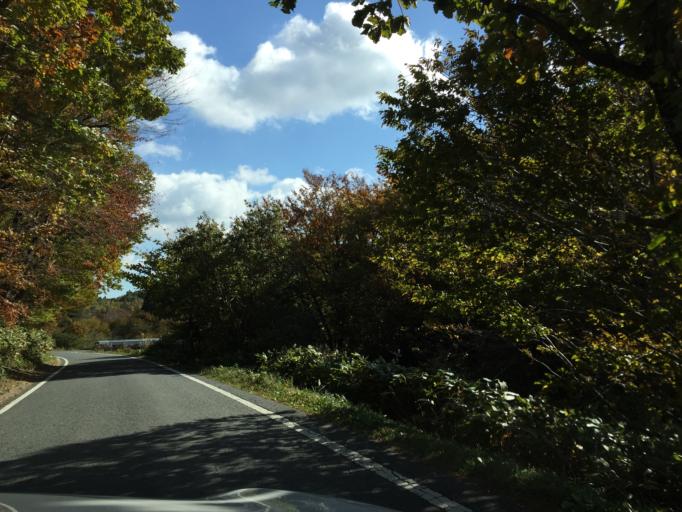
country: JP
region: Fukushima
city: Funehikimachi-funehiki
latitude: 37.2937
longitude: 140.7332
